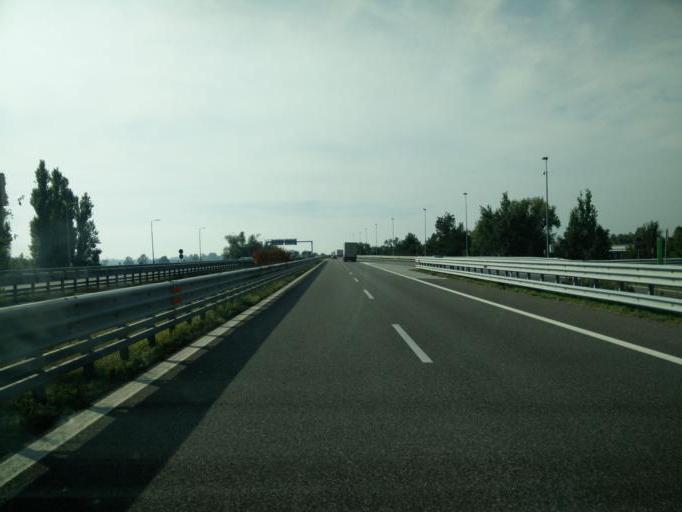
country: IT
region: Lombardy
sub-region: Provincia di Cremona
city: San Felice
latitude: 45.1395
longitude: 10.0707
